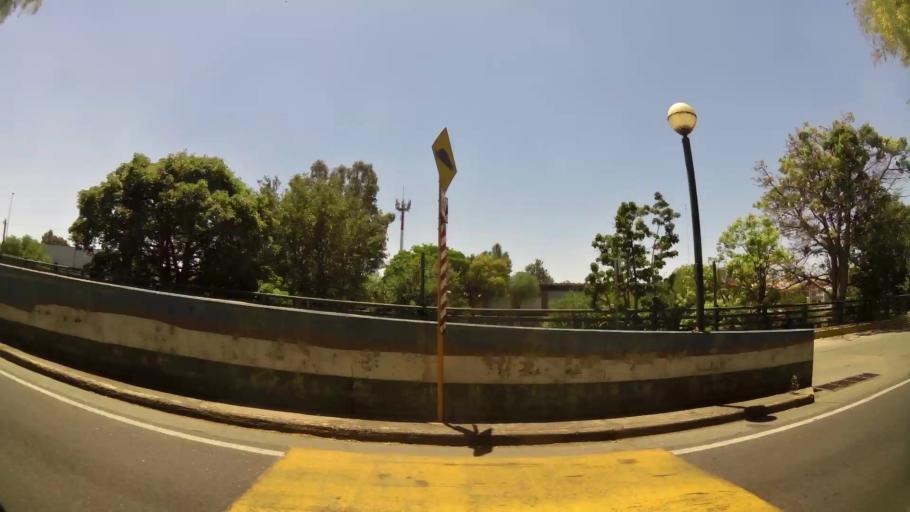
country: AR
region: Cordoba
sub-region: Departamento de Capital
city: Cordoba
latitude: -31.3928
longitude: -64.2051
